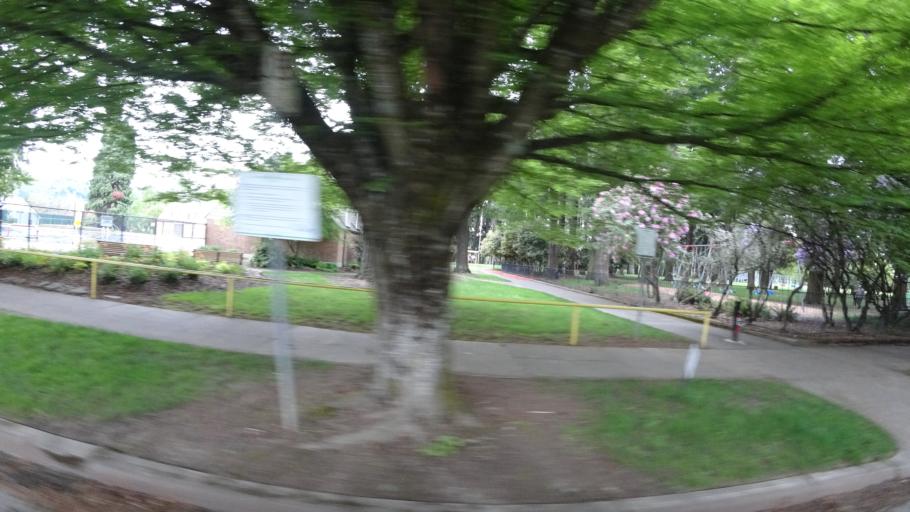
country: US
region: Oregon
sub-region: Clackamas County
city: Milwaukie
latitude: 45.4668
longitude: -122.6590
